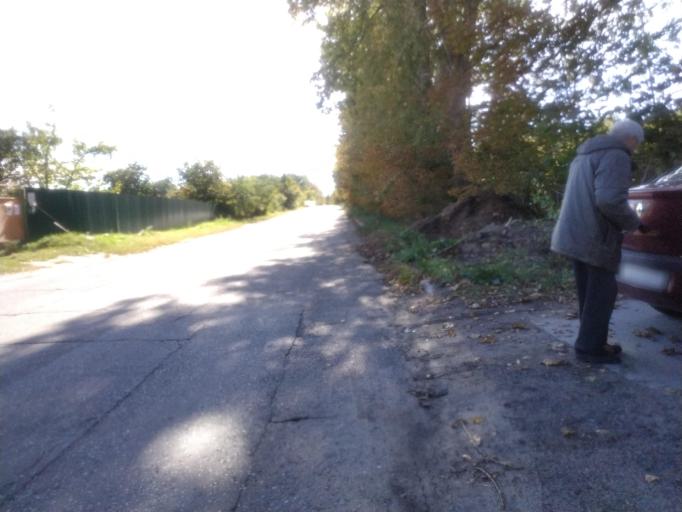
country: RU
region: Chuvashia
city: Novyye Lapsary
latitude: 56.1416
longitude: 47.1430
